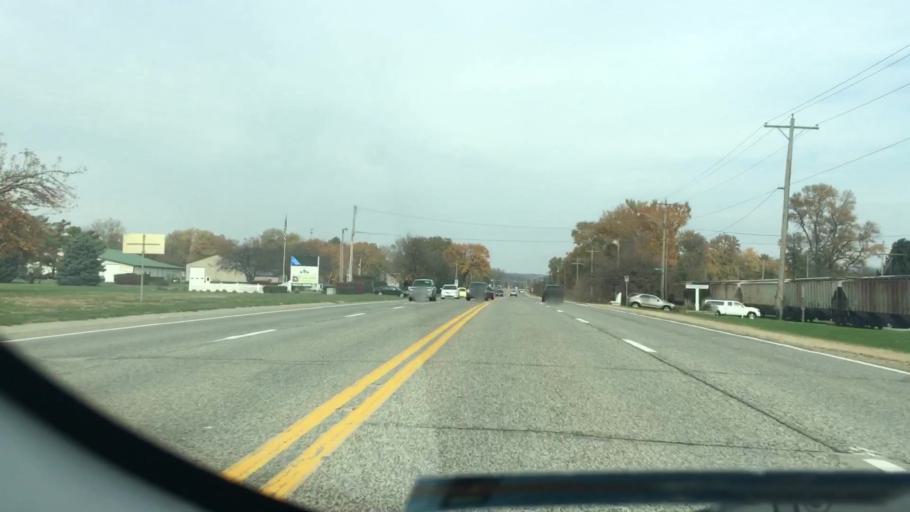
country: US
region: Illinois
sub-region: Peoria County
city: Peoria Heights
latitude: 40.7532
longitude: -89.5616
